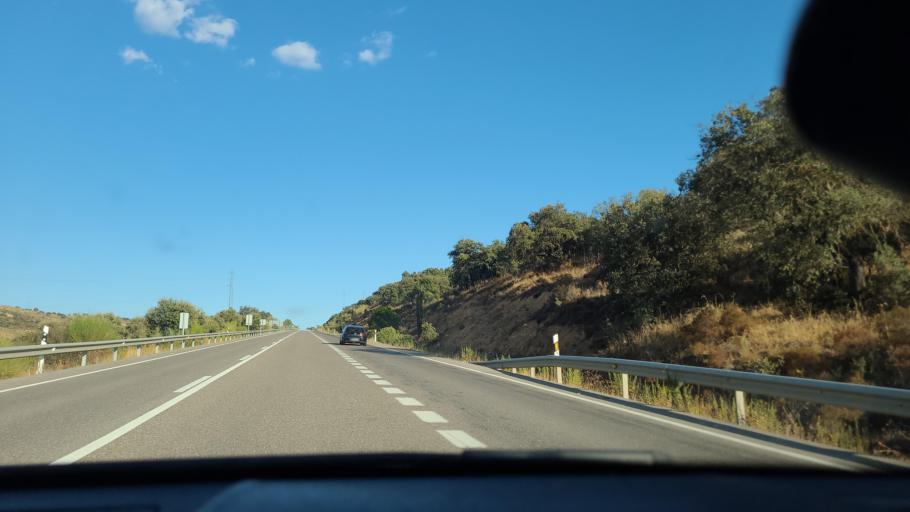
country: ES
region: Andalusia
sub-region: Province of Cordoba
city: Espiel
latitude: 38.1813
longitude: -5.0256
